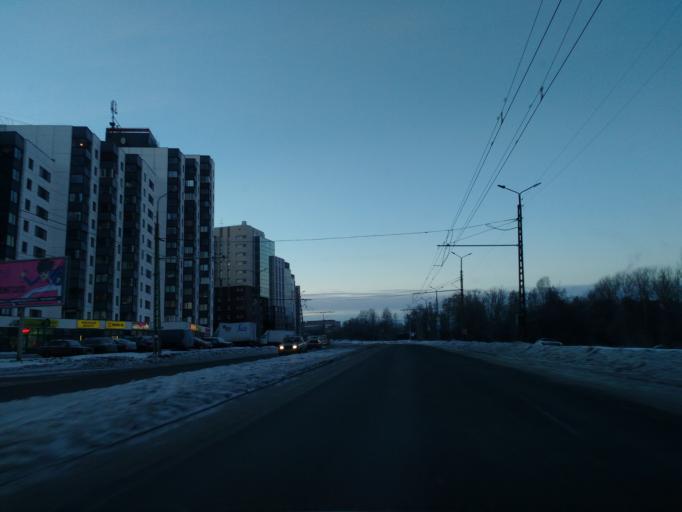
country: RU
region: Republic of Karelia
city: Petrozavodsk
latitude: 61.8097
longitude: 34.3318
